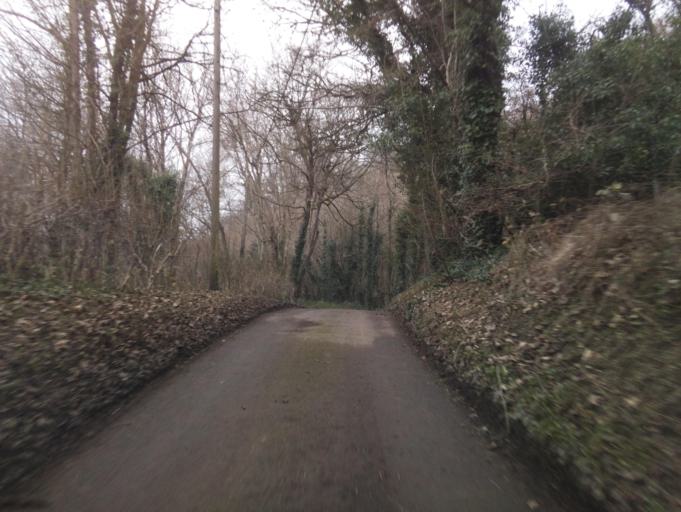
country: GB
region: England
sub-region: Wiltshire
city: Biddestone
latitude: 51.4624
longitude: -2.2267
